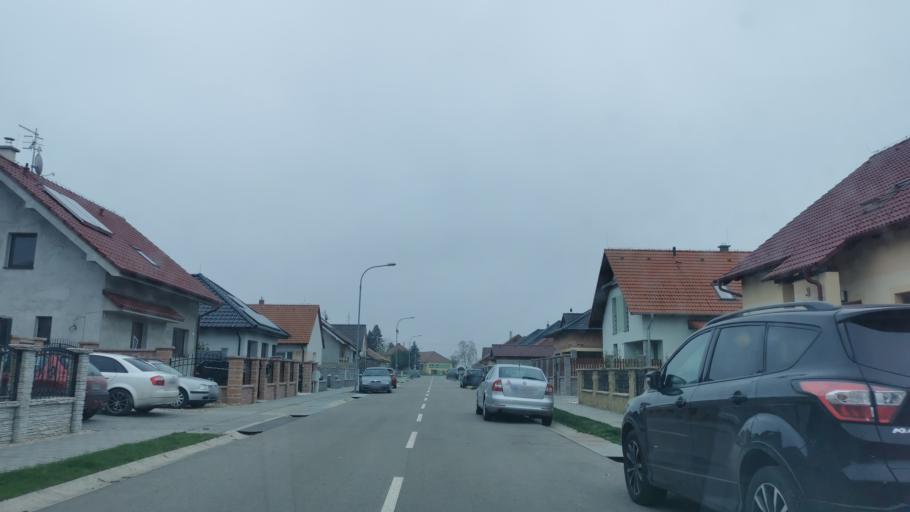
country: SK
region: Trnavsky
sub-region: Okres Skalica
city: Holic
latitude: 48.8318
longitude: 17.1658
